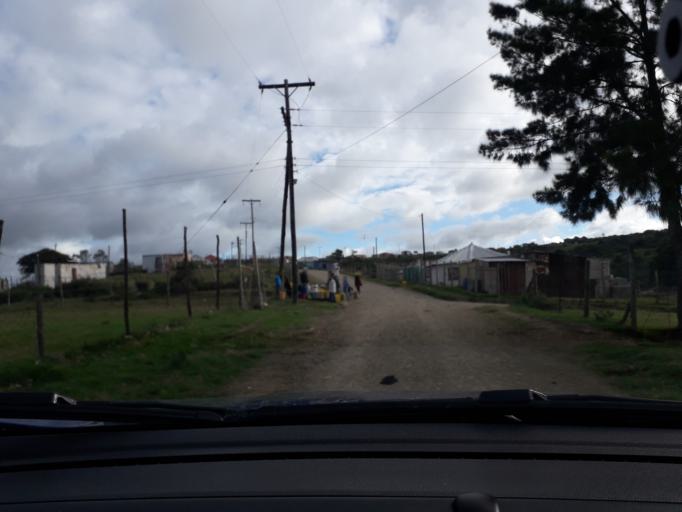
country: ZA
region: Eastern Cape
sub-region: Buffalo City Metropolitan Municipality
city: East London
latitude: -32.8047
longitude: 27.9612
